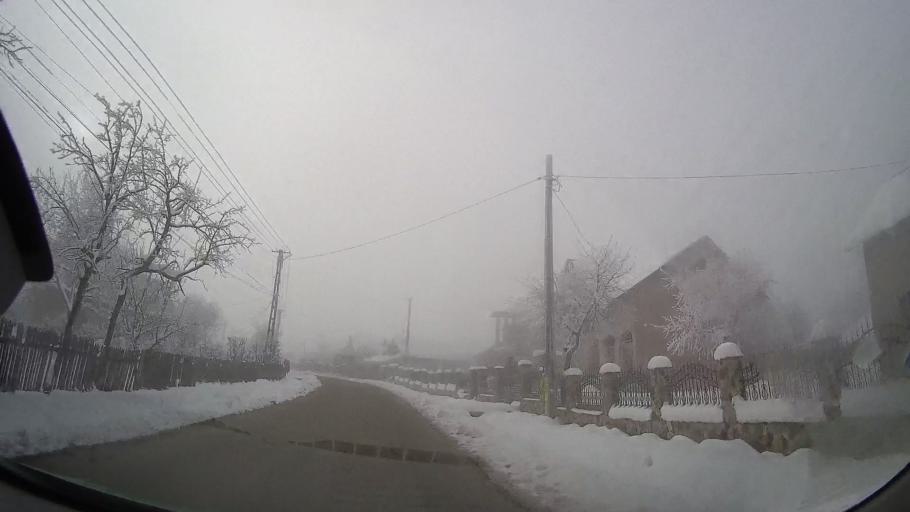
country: RO
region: Iasi
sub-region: Comuna Valea Seaca
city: Topile
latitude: 47.2642
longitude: 26.6680
